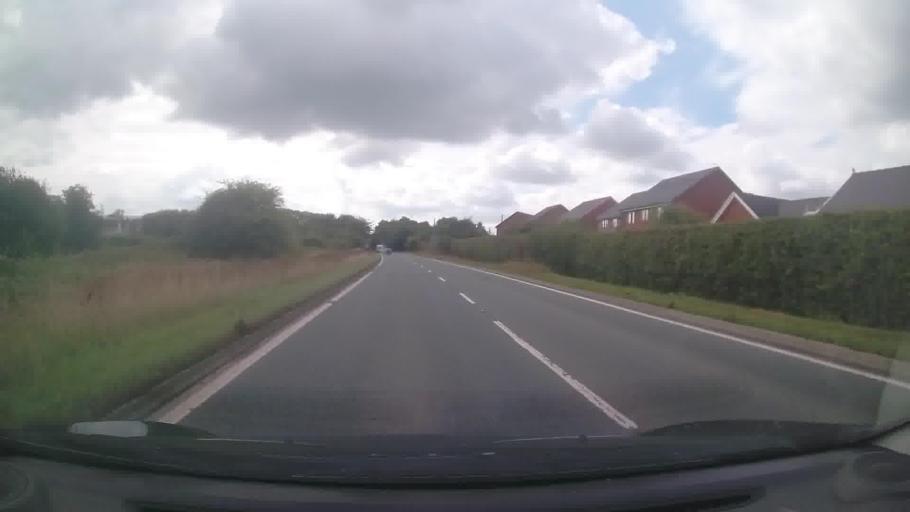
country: GB
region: England
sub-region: Shropshire
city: Pant
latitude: 52.7366
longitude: -3.0958
